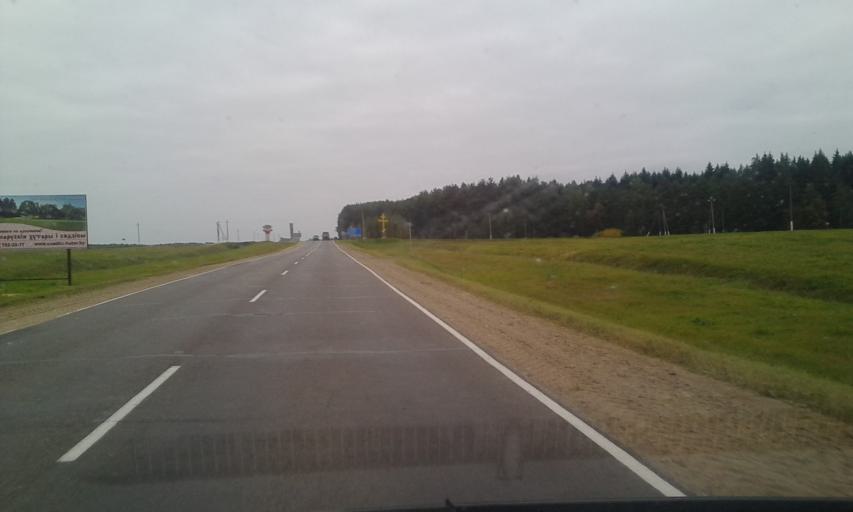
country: BY
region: Vitebsk
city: Pastavy
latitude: 55.1047
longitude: 26.8744
